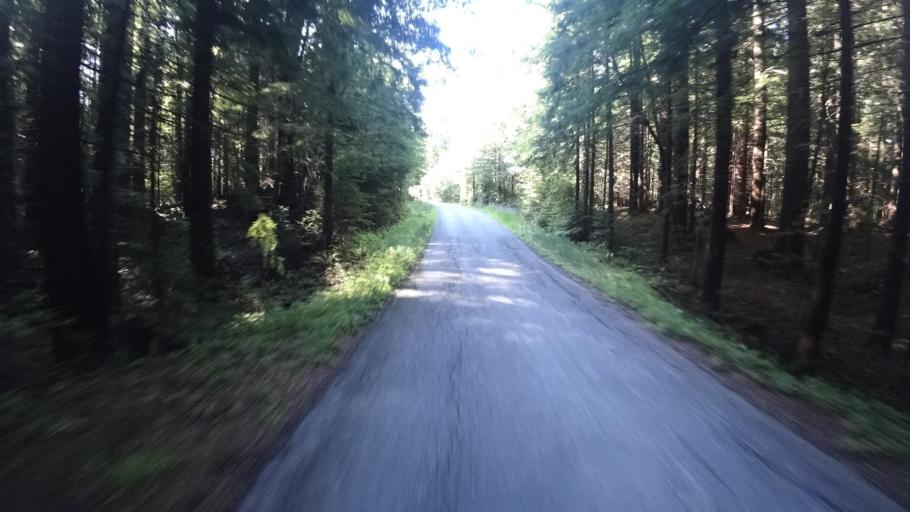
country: US
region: California
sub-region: Humboldt County
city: Rio Dell
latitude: 40.4388
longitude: -123.9703
